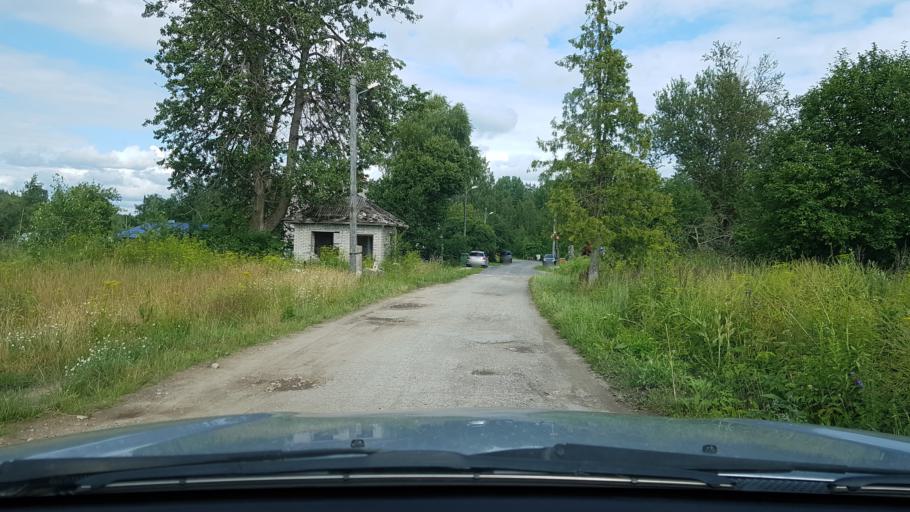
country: EE
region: Ida-Virumaa
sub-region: Narva-Joesuu linn
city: Narva-Joesuu
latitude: 59.4489
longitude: 28.0788
